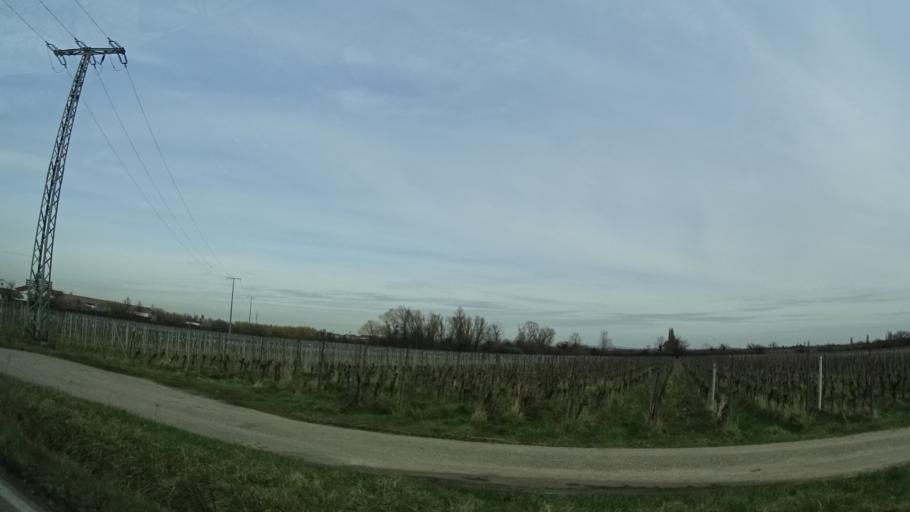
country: DE
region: Rheinland-Pfalz
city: Neustadt
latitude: 49.3356
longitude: 8.1518
